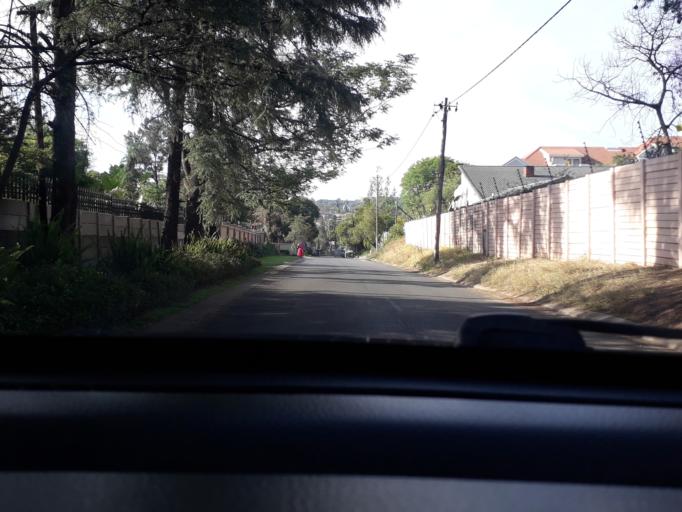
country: ZA
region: Gauteng
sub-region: City of Johannesburg Metropolitan Municipality
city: Midrand
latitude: -26.0631
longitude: 28.0636
